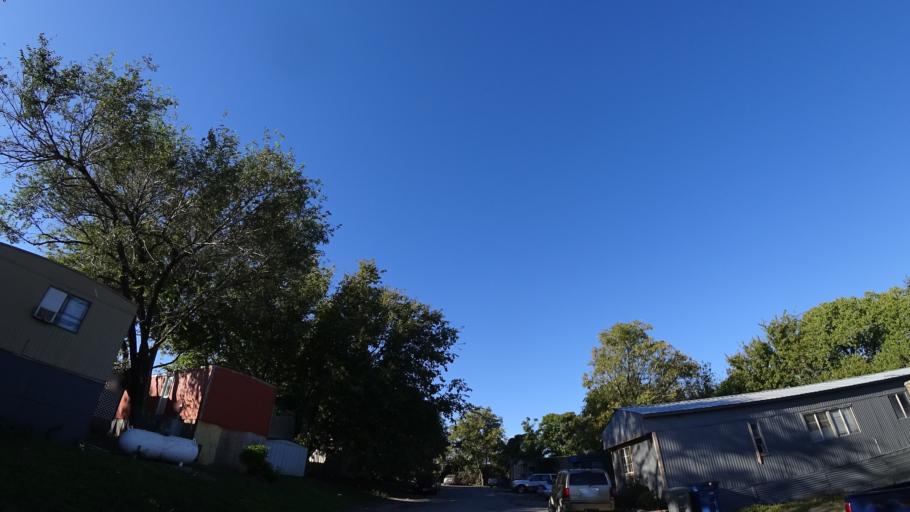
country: US
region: Texas
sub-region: Travis County
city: Austin
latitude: 30.2185
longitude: -97.6946
